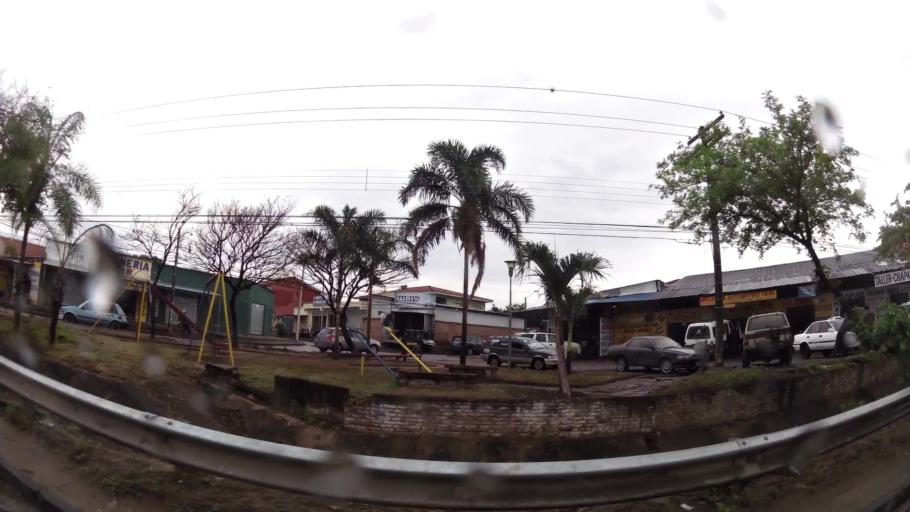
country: BO
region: Santa Cruz
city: Santa Cruz de la Sierra
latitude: -17.8112
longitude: -63.1939
